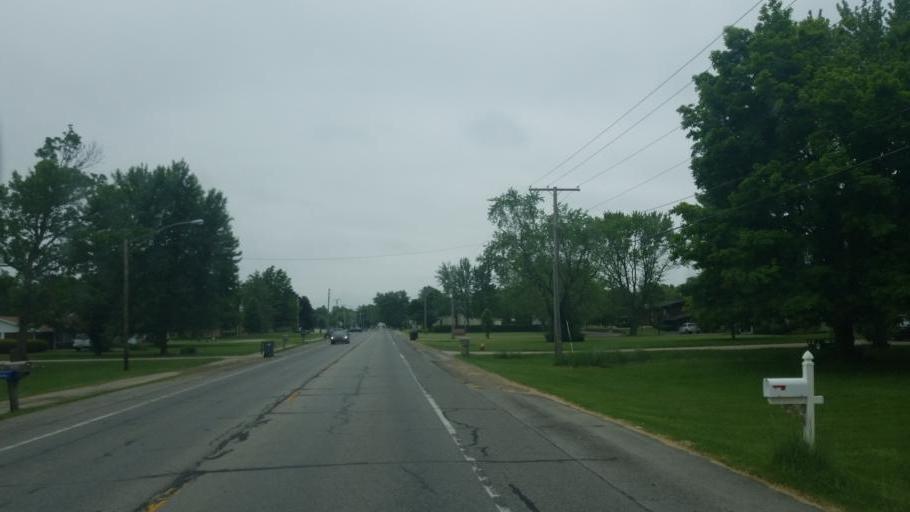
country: US
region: Indiana
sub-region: Elkhart County
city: Nappanee
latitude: 41.4545
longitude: -86.0015
